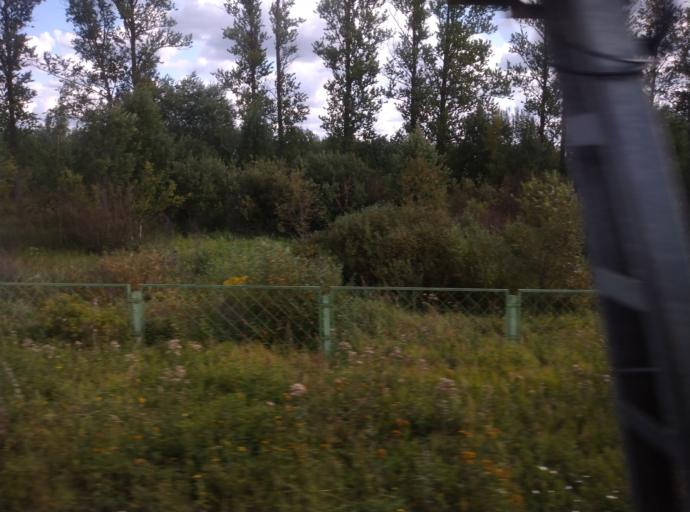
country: RU
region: St.-Petersburg
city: Kolpino
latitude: 59.7405
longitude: 30.6258
